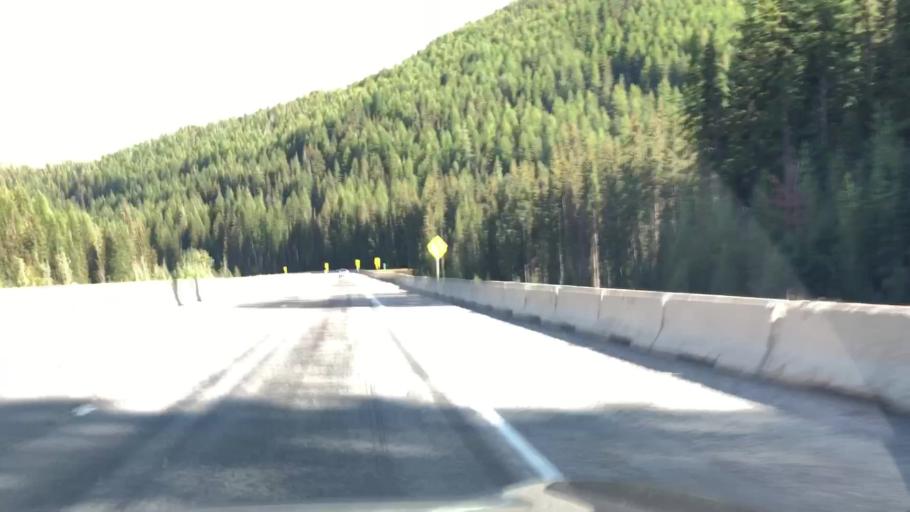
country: US
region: Idaho
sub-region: Shoshone County
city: Wallace
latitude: 47.4347
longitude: -115.6742
